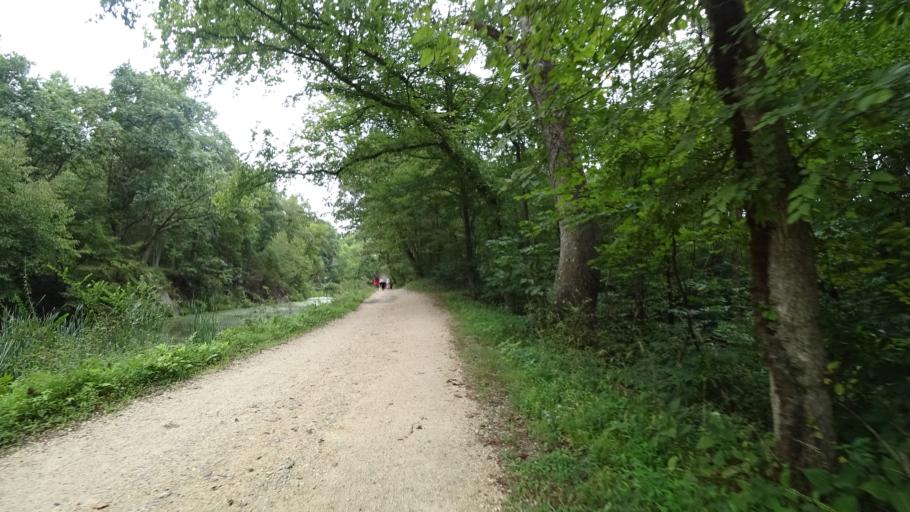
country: US
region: Maryland
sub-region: Montgomery County
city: Potomac
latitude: 38.9774
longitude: -77.2207
